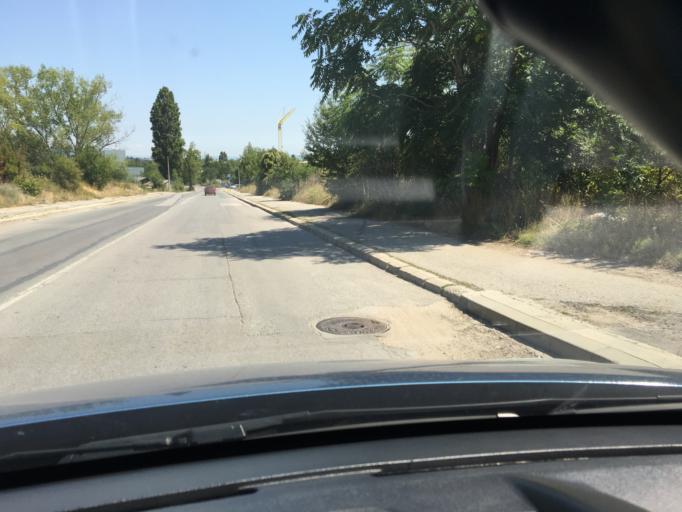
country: BG
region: Sofia-Capital
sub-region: Stolichna Obshtina
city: Sofia
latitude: 42.6370
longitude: 23.3980
